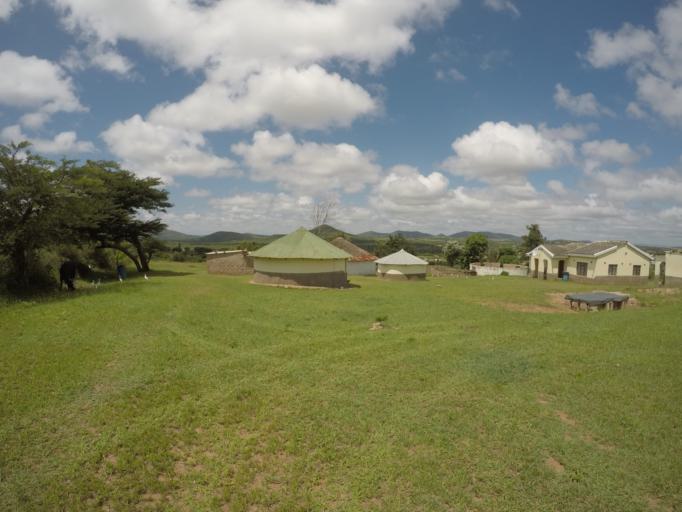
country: ZA
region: KwaZulu-Natal
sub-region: uThungulu District Municipality
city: Empangeni
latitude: -28.5803
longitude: 31.8409
